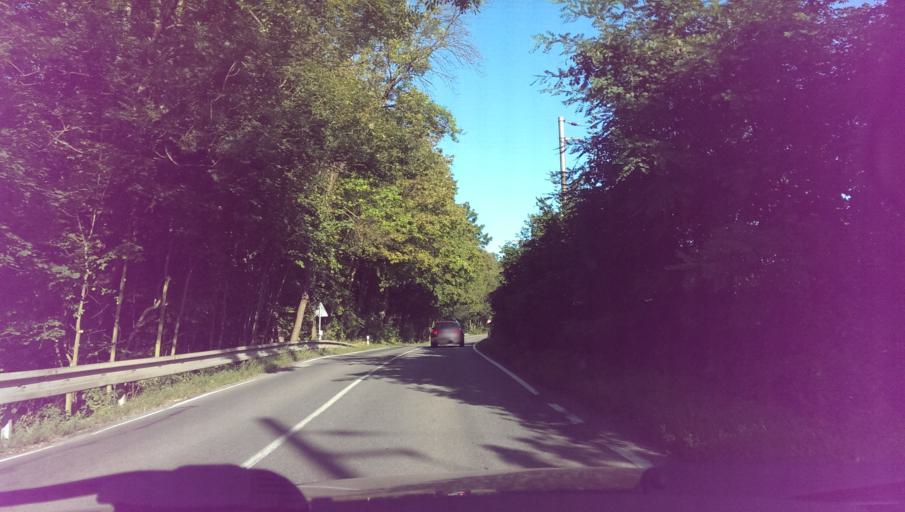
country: CZ
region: Olomoucky
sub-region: Okres Prerov
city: Hranice
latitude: 49.5268
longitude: 17.7512
